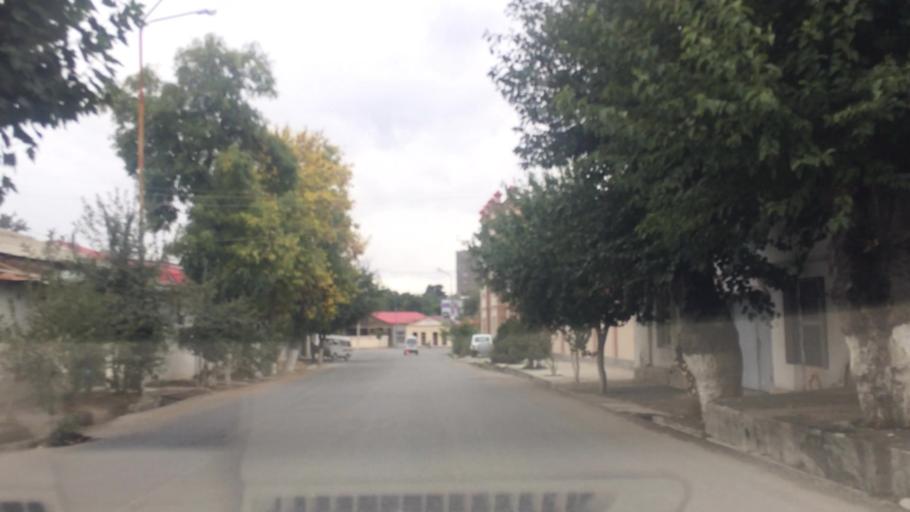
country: UZ
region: Samarqand
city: Samarqand
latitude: 39.6586
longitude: 66.9719
